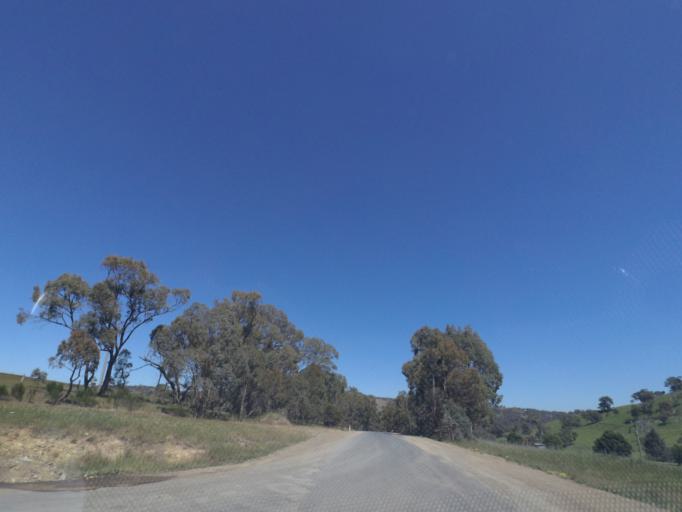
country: AU
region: Victoria
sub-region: Whittlesea
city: Whittlesea
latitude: -37.2885
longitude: 144.9948
